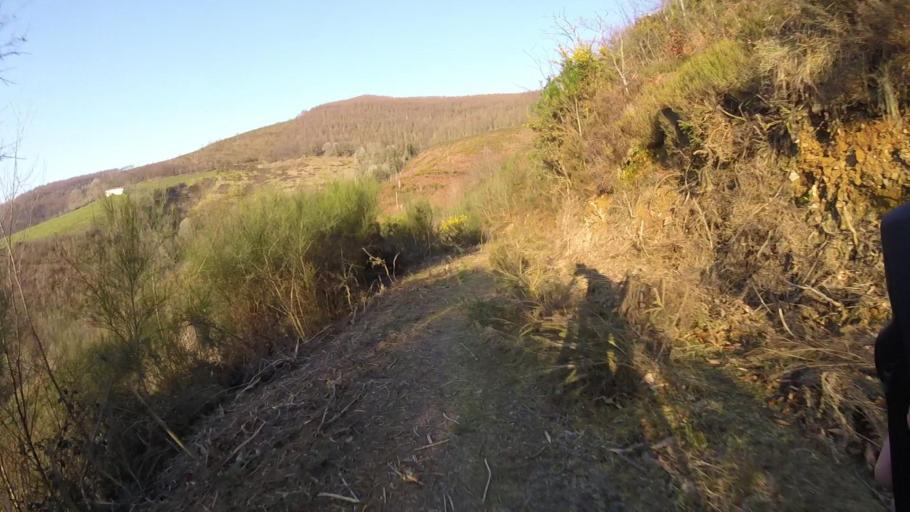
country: ES
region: Navarre
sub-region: Provincia de Navarra
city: Arano
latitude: 43.2283
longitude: -1.8623
